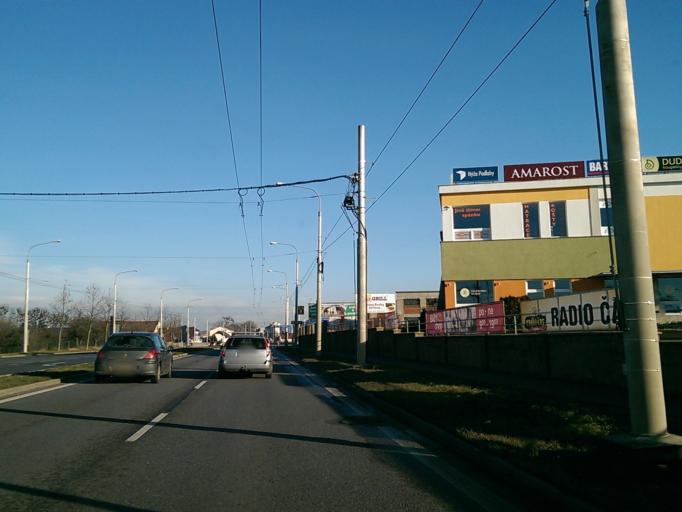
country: CZ
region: Zlin
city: Tecovice
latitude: 49.2090
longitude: 17.5925
